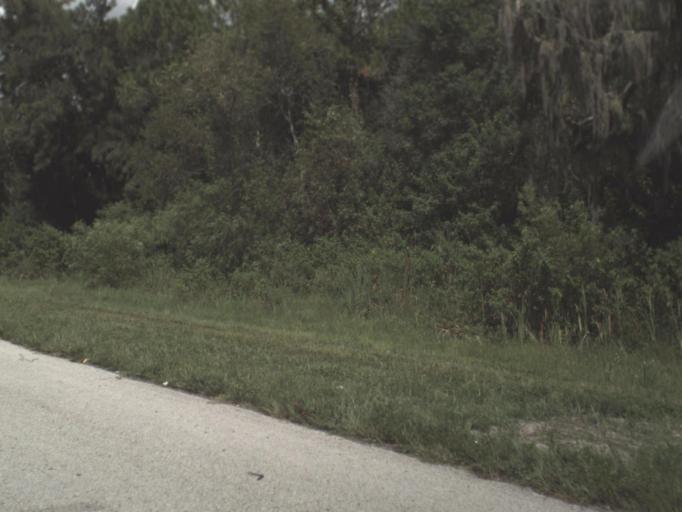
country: US
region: Florida
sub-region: Hillsborough County
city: Ruskin
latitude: 27.6966
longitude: -82.4063
